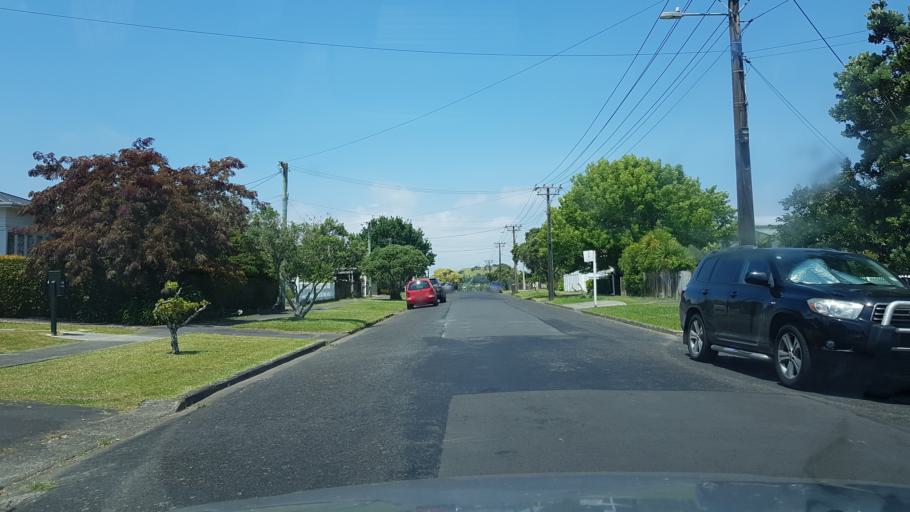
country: NZ
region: Auckland
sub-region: Auckland
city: North Shore
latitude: -36.8102
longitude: 174.7950
